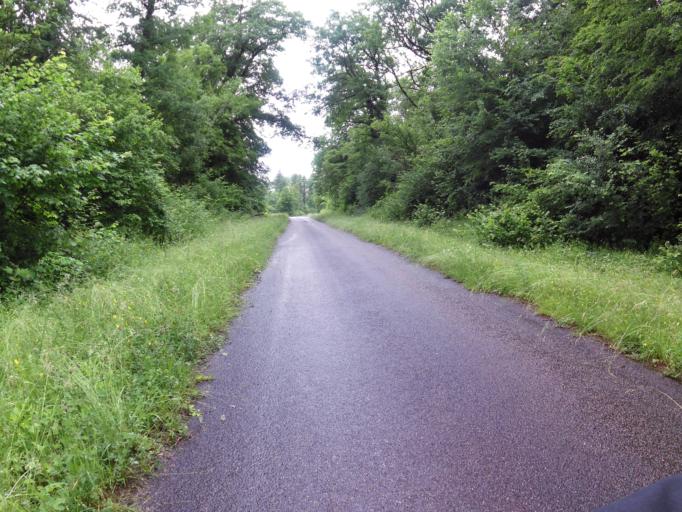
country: FR
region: Champagne-Ardenne
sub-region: Departement de la Marne
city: Sermaize-les-Bains
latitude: 48.7530
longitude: 4.9597
